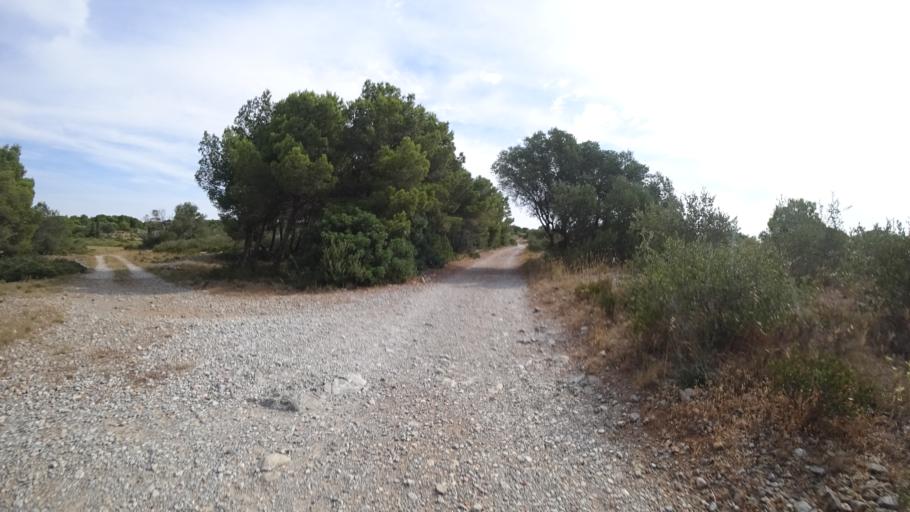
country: FR
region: Languedoc-Roussillon
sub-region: Departement de l'Aude
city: Leucate
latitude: 42.8967
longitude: 3.0334
